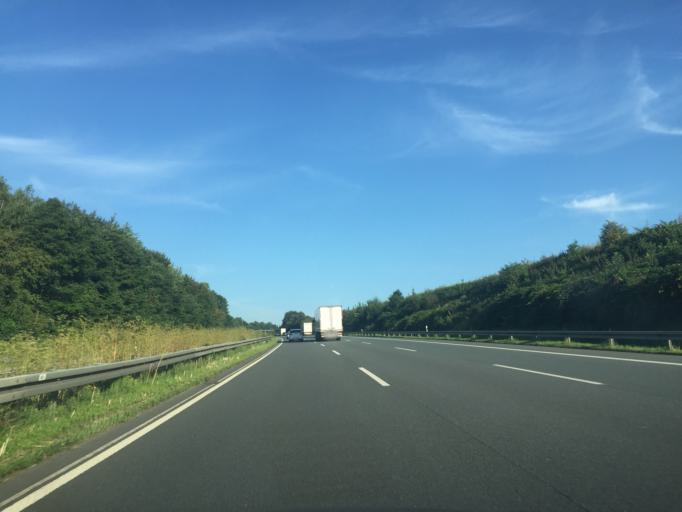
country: DE
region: North Rhine-Westphalia
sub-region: Regierungsbezirk Arnsberg
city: Olpe
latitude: 51.0354
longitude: 7.8163
